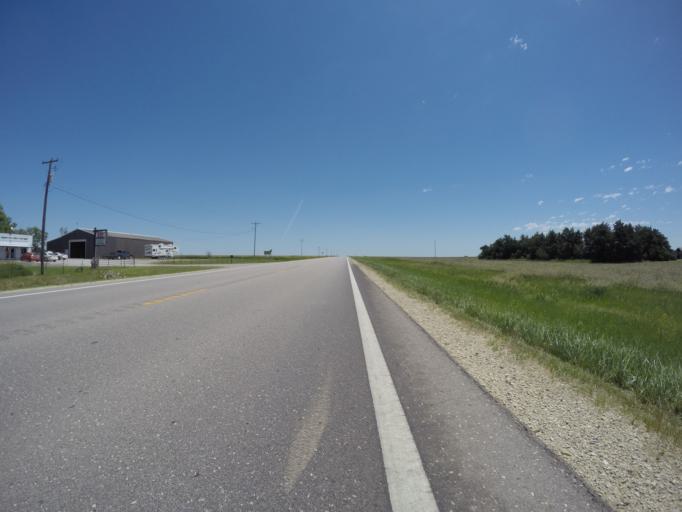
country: US
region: Kansas
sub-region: Republic County
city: Belleville
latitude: 39.8127
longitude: -97.6860
